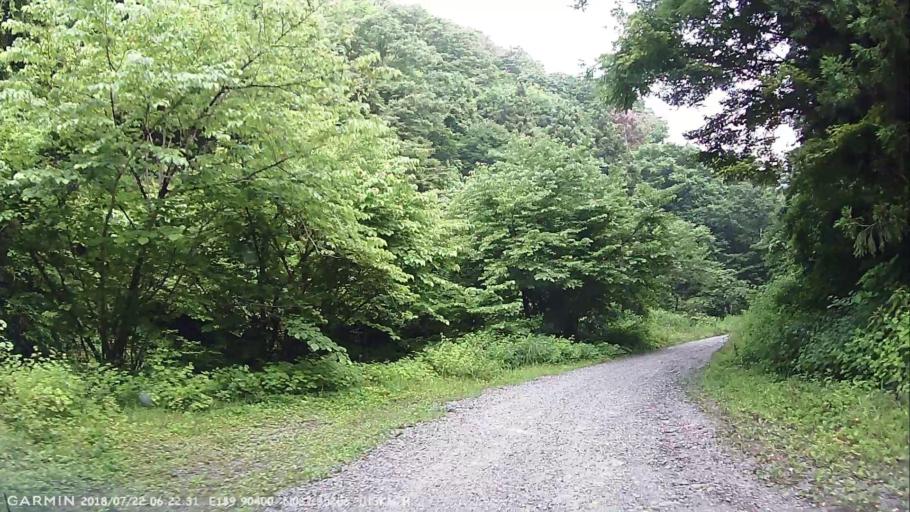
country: JP
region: Fukushima
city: Kitakata
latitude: 37.3520
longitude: 139.9042
